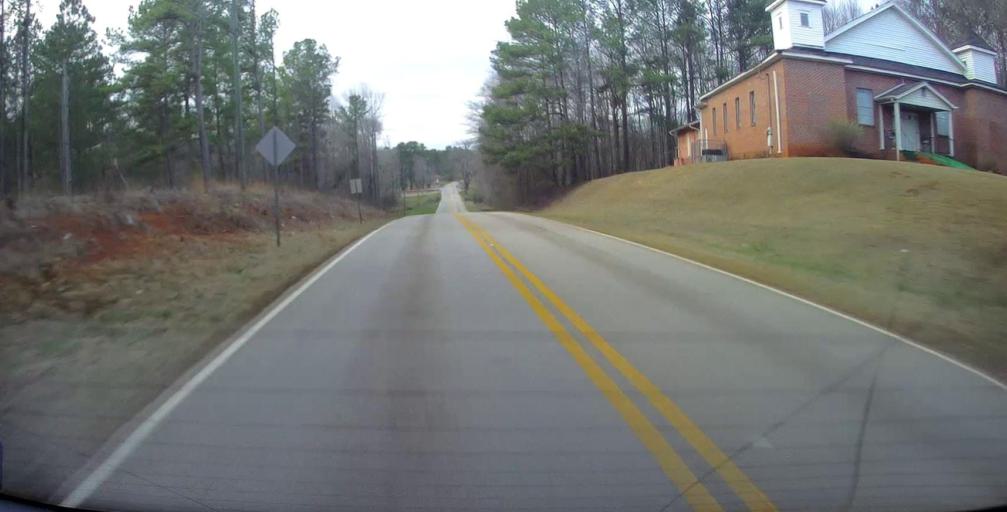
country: US
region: Georgia
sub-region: Troup County
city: West Point
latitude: 32.9427
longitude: -85.1314
